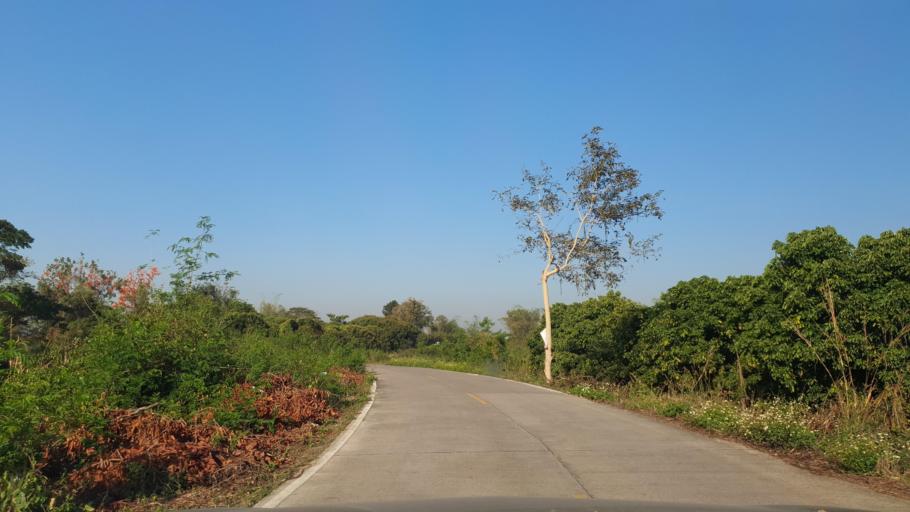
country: TH
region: Chiang Mai
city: Saraphi
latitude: 18.6818
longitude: 99.0784
